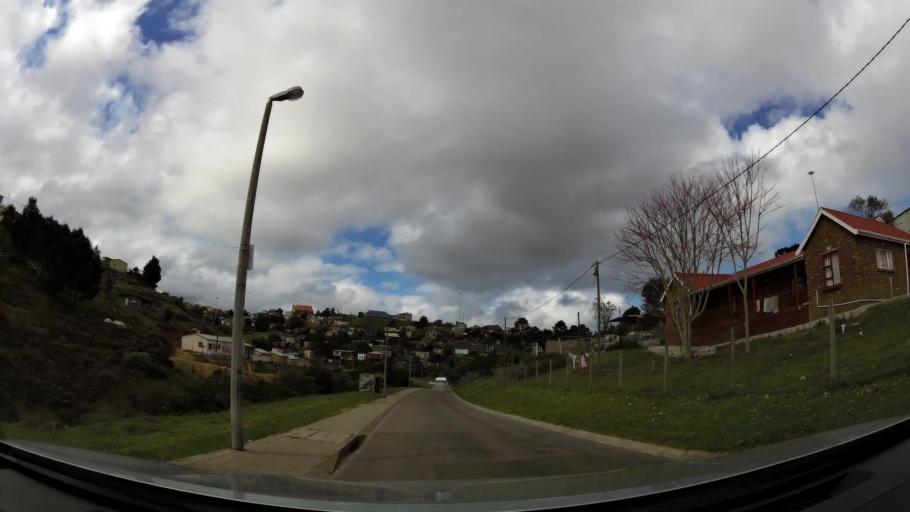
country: ZA
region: Western Cape
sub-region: Eden District Municipality
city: Knysna
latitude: -34.0338
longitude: 23.0998
